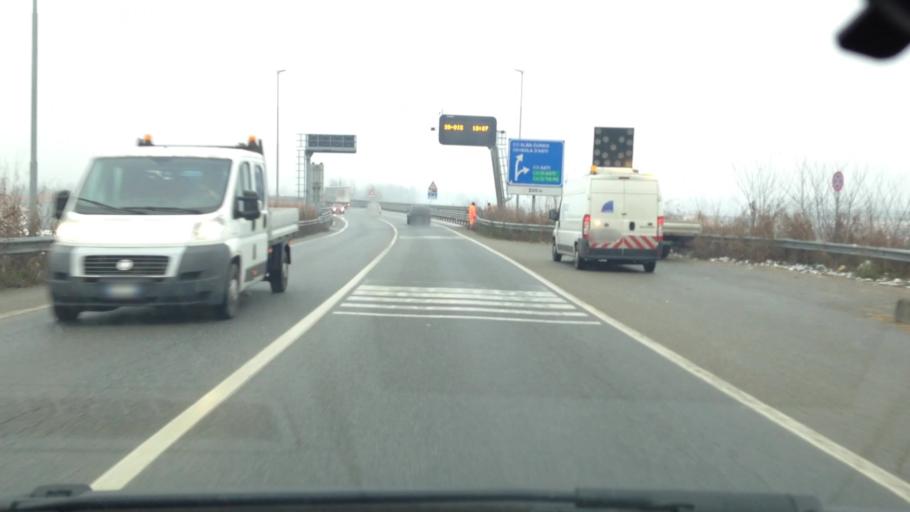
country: IT
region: Piedmont
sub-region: Provincia di Asti
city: Isola d'Asti
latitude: 44.8421
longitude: 8.1936
